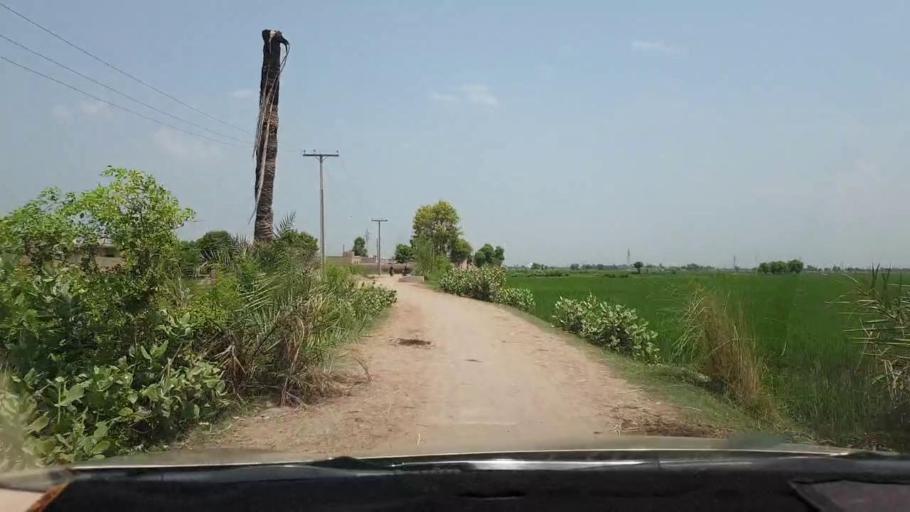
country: PK
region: Sindh
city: Naudero
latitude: 27.6610
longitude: 68.3240
